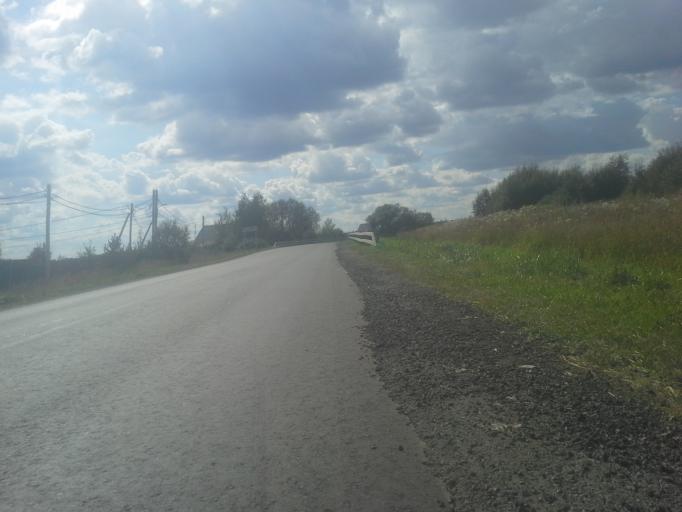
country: RU
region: Moskovskaya
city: Selyatino
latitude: 55.3254
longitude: 37.0961
